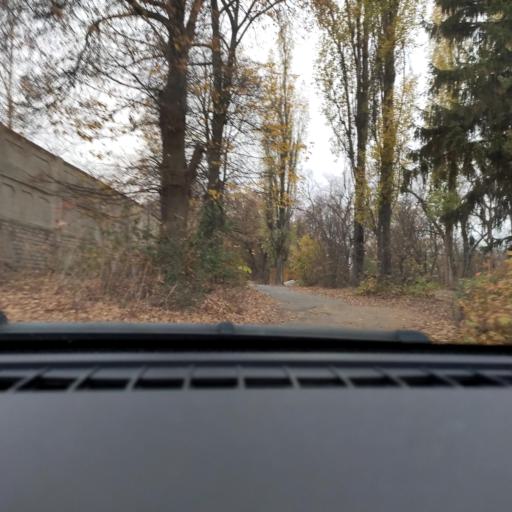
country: RU
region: Voronezj
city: Voronezh
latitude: 51.7179
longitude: 39.2331
